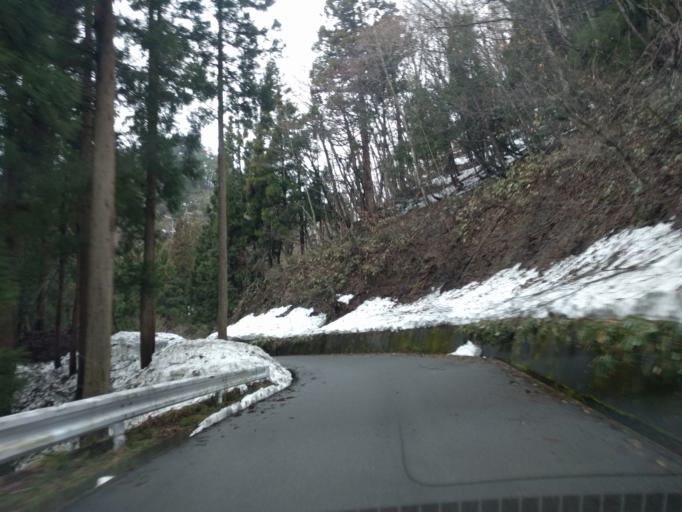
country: JP
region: Fukushima
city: Kitakata
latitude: 37.6908
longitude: 139.9467
